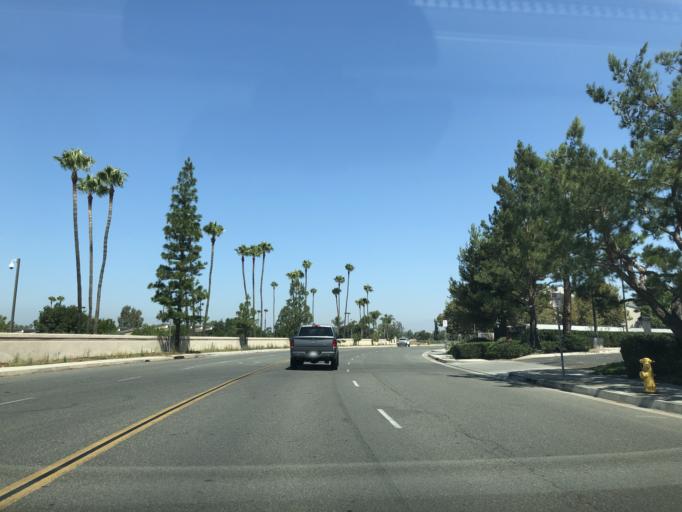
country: US
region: California
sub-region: Riverside County
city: Corona
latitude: 33.8987
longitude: -117.5653
